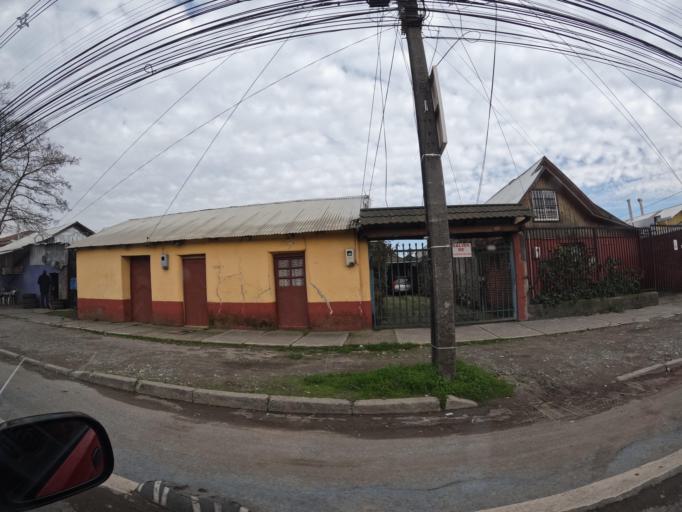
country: CL
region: Maule
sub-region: Provincia de Linares
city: Linares
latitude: -35.8422
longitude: -71.5852
